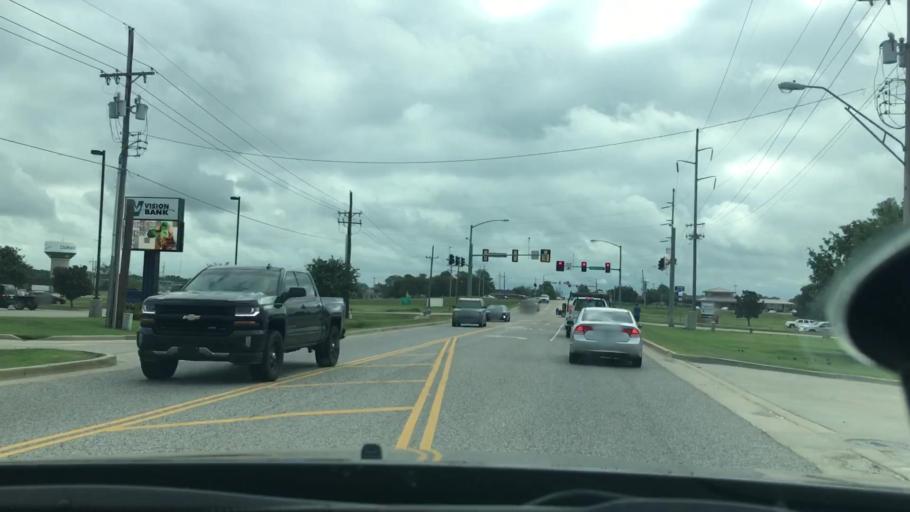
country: US
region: Oklahoma
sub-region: Bryan County
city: Durant
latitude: 34.0049
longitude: -96.4029
